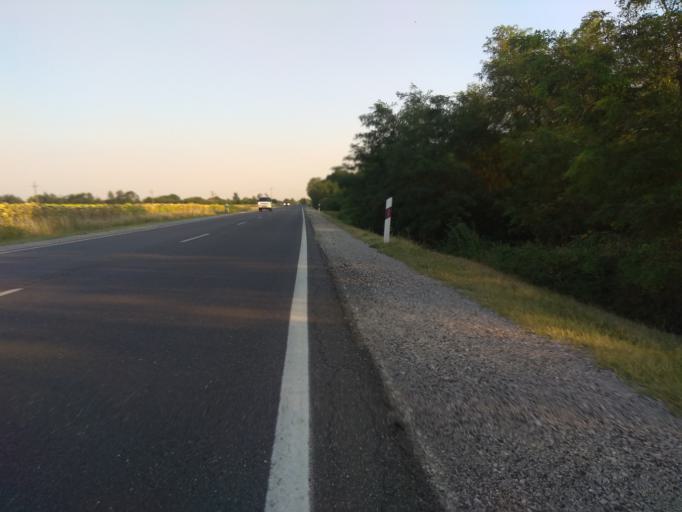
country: HU
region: Borsod-Abauj-Zemplen
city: Nyekladhaza
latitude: 47.9690
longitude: 20.8315
